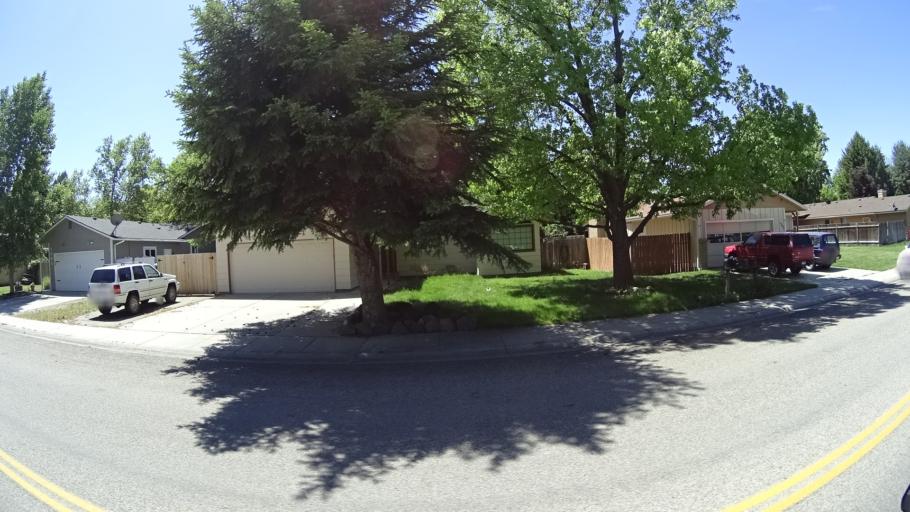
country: US
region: Idaho
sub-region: Ada County
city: Boise
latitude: 43.5678
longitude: -116.1663
